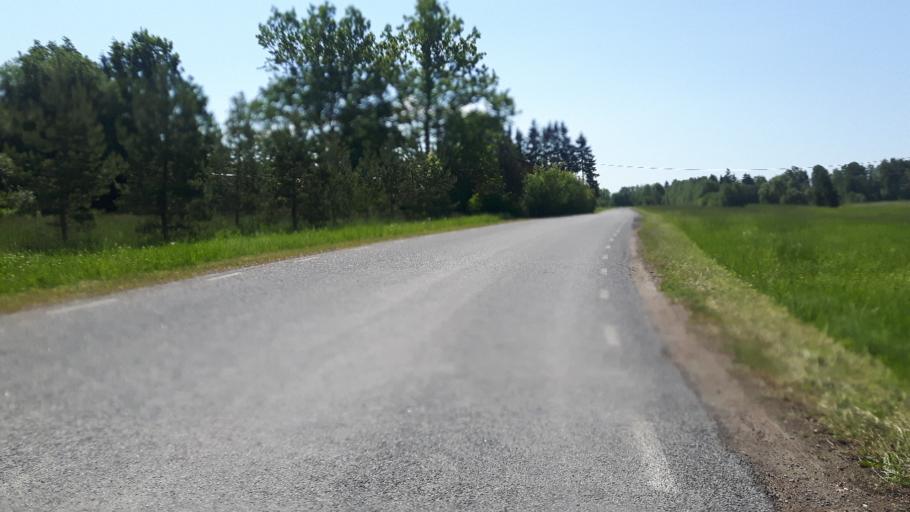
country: EE
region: Paernumaa
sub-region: Vaendra vald (alev)
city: Vandra
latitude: 58.6040
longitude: 25.0224
